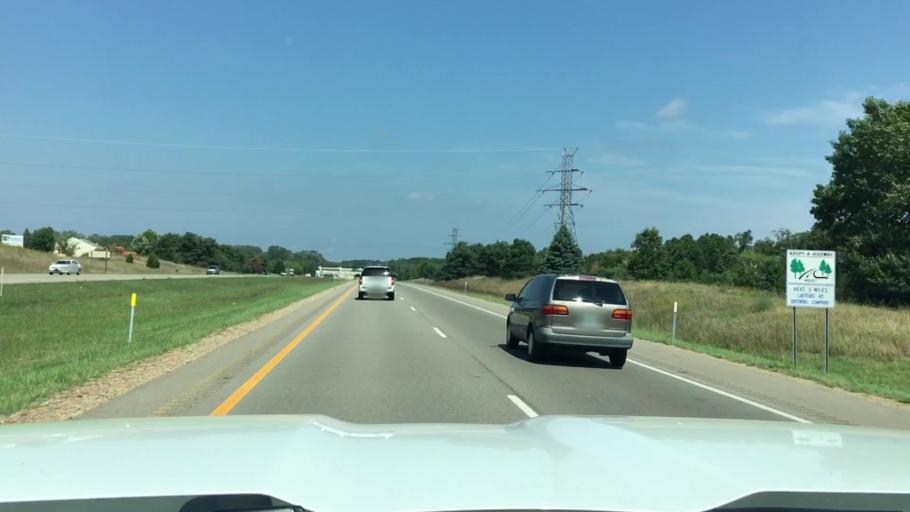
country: US
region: Michigan
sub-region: Kalamazoo County
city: Portage
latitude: 42.2227
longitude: -85.6403
